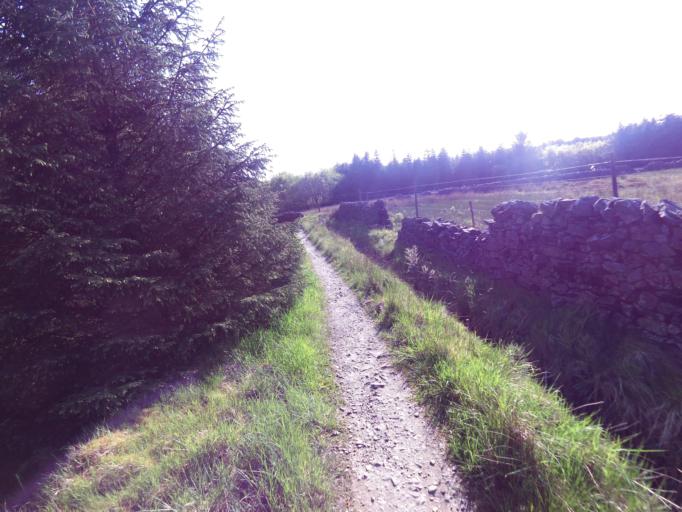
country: GB
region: England
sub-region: North Yorkshire
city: Settle
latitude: 54.0237
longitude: -2.3836
